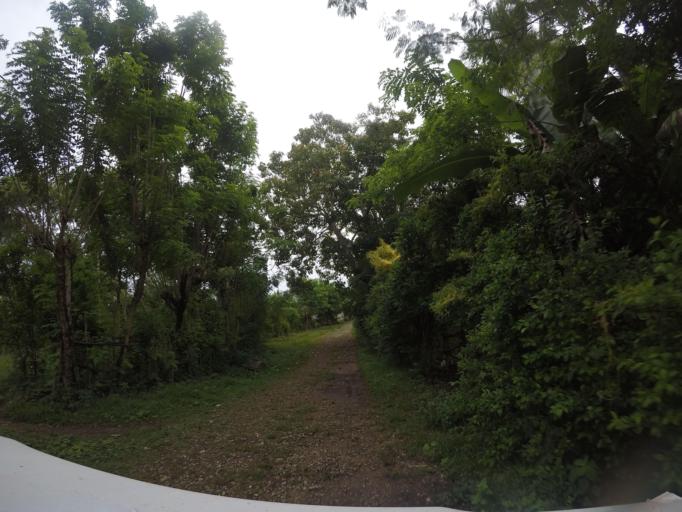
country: TL
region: Lautem
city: Lospalos
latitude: -8.5302
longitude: 127.0038
